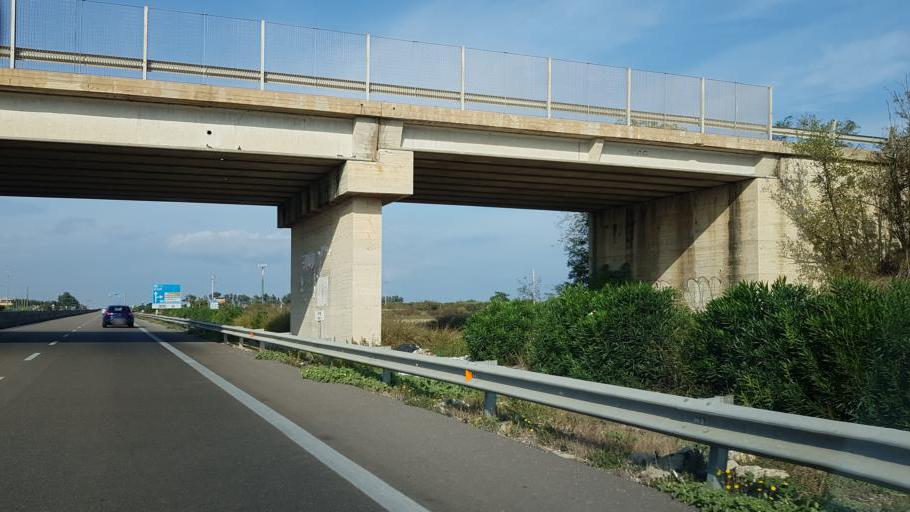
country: IT
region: Apulia
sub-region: Provincia di Brindisi
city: San Vito dei Normanni
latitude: 40.6893
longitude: 17.8246
